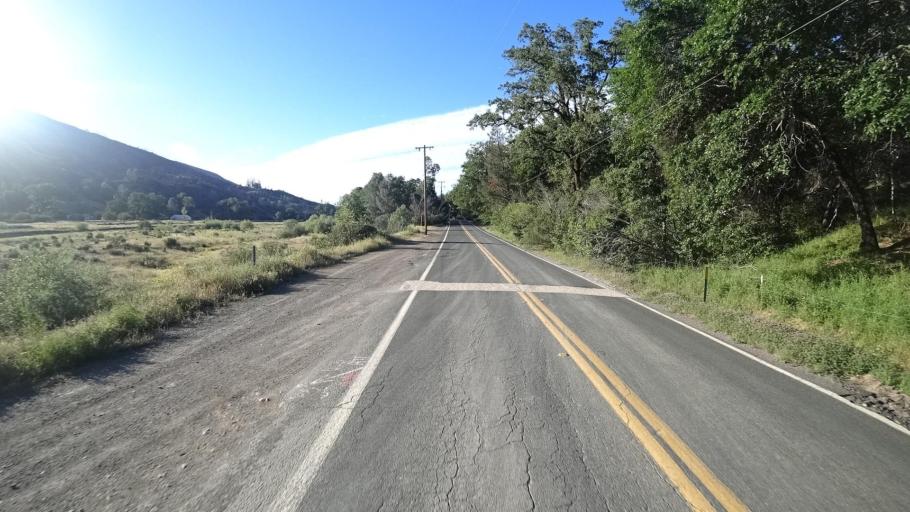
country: US
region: California
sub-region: Lake County
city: Upper Lake
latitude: 39.2308
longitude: -122.9447
